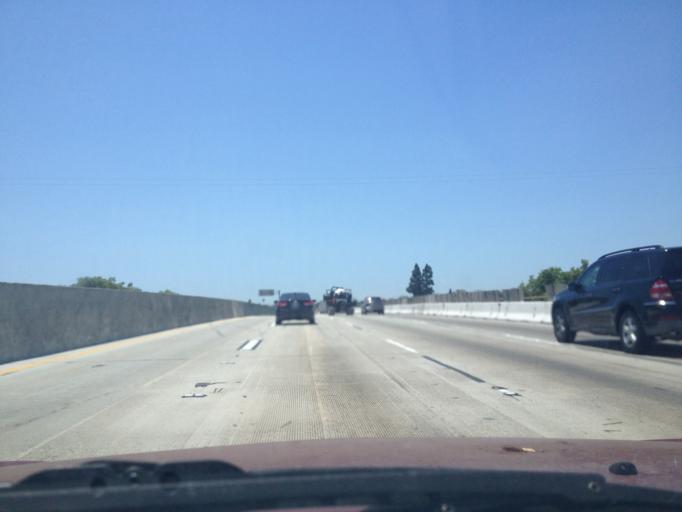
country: US
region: California
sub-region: Orange County
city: Fullerton
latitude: 33.8541
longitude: -117.9415
